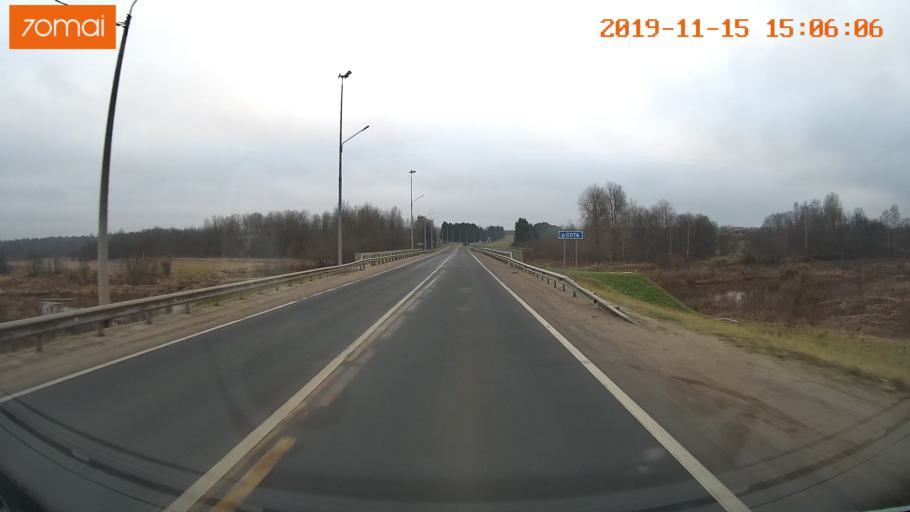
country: RU
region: Jaroslavl
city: Prechistoye
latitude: 58.3964
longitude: 40.3151
